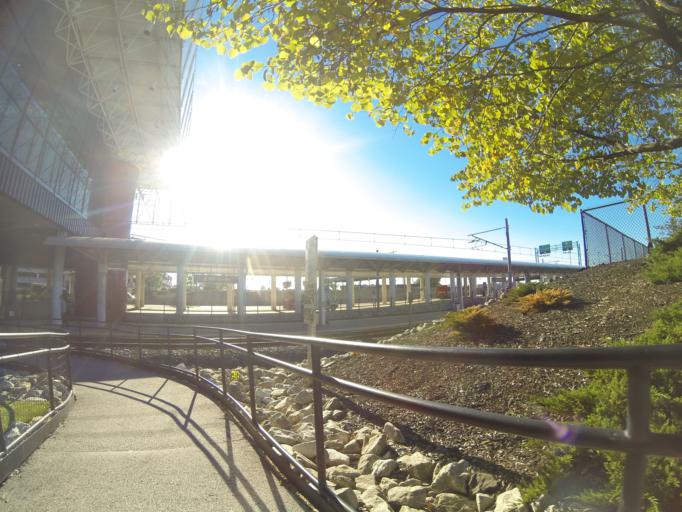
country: US
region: Maryland
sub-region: Anne Arundel County
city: Linthicum
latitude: 39.1826
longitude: -76.6693
